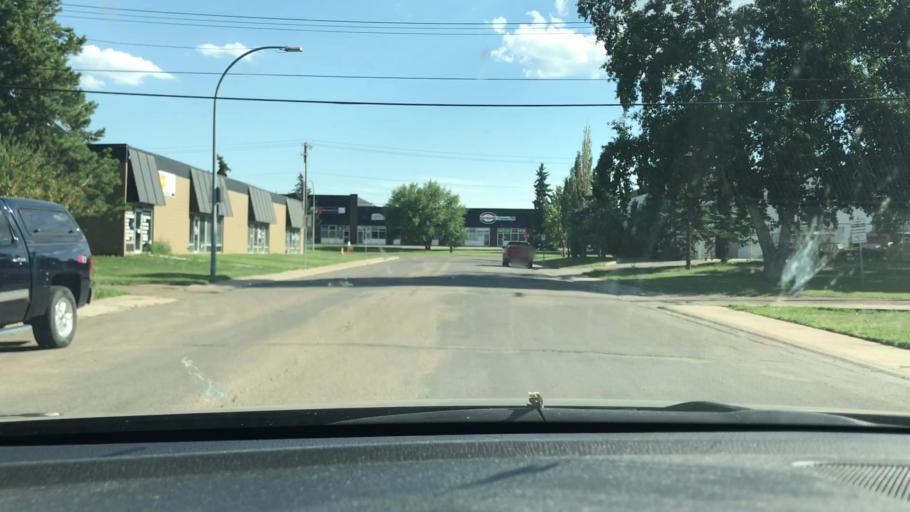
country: CA
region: Alberta
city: Edmonton
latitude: 53.5190
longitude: -113.4228
